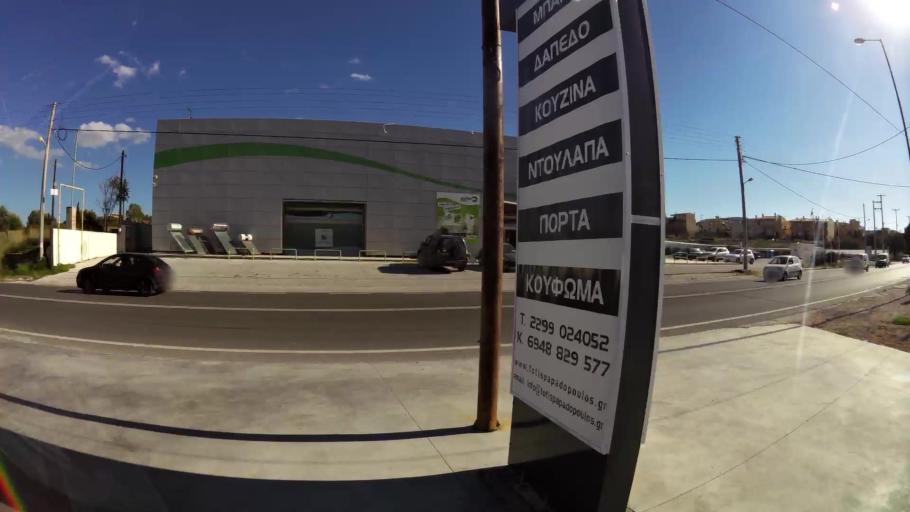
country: GR
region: Attica
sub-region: Nomarchia Anatolikis Attikis
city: Markopoulo
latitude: 37.8916
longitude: 23.9458
